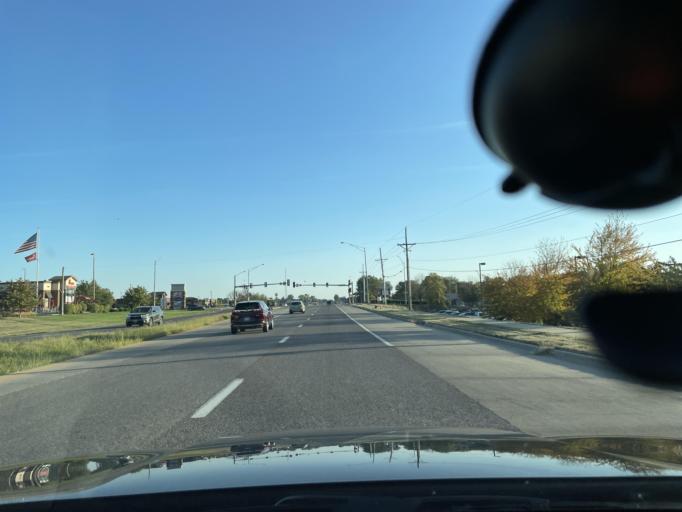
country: US
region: Missouri
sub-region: Andrew County
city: Country Club Village
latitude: 39.8153
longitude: -94.8153
